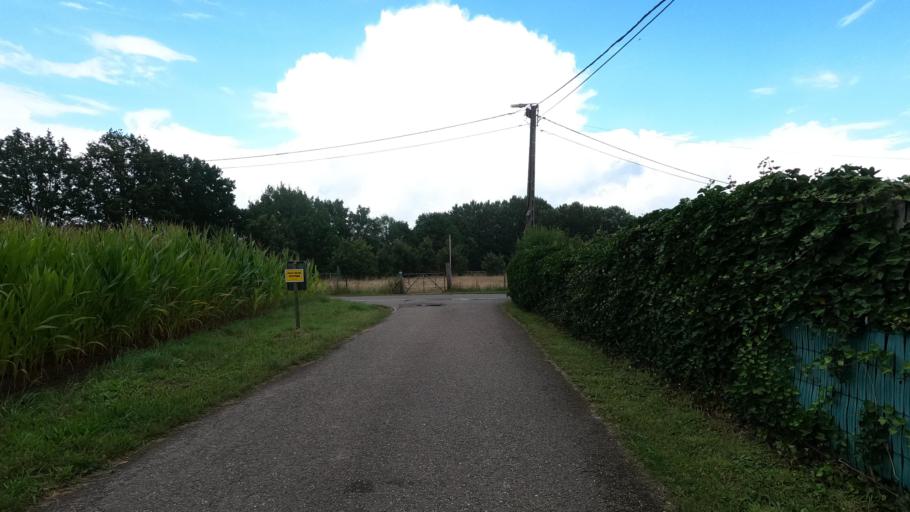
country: BE
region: Flanders
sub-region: Provincie Vlaams-Brabant
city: Tremelo
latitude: 50.9779
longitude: 4.6931
